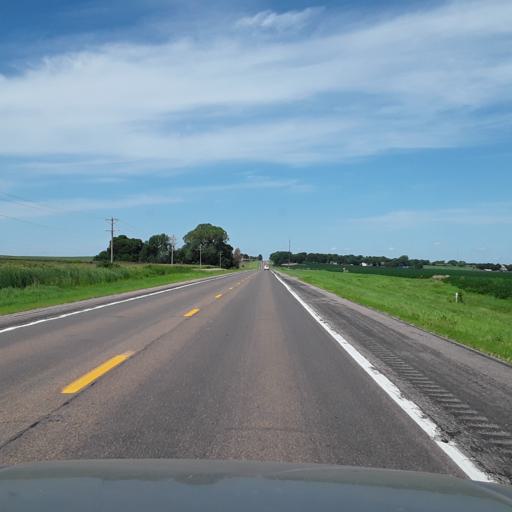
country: US
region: Nebraska
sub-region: Seward County
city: Seward
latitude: 40.9017
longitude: -97.1299
